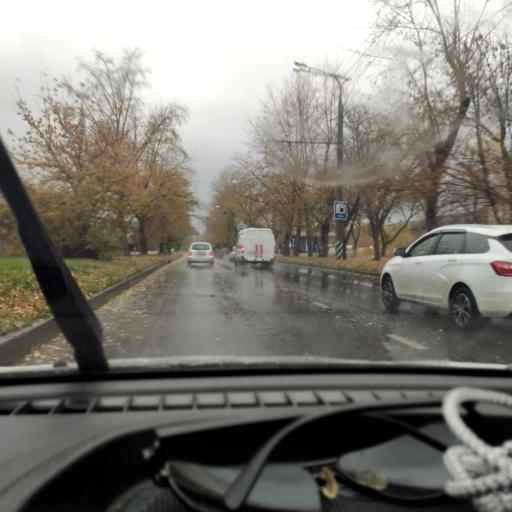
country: RU
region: Samara
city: Tol'yatti
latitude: 53.5157
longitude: 49.4374
